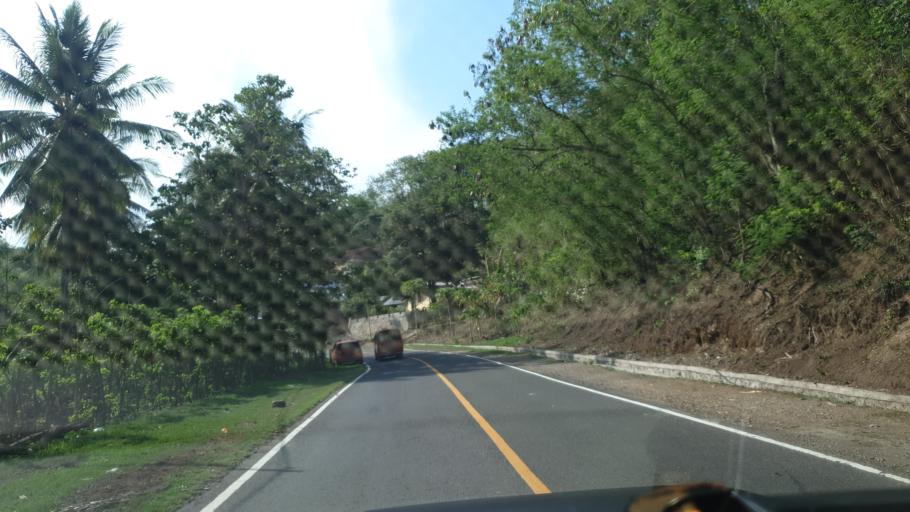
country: ID
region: East Nusa Tenggara
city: Nangalimang
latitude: -8.6582
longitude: 122.2016
